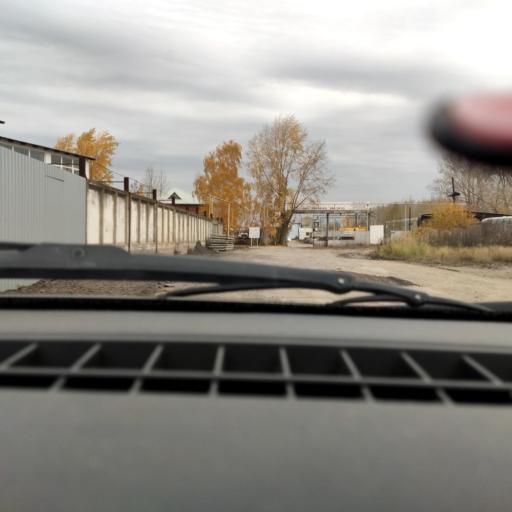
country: RU
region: Bashkortostan
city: Ufa
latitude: 54.8340
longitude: 56.1167
